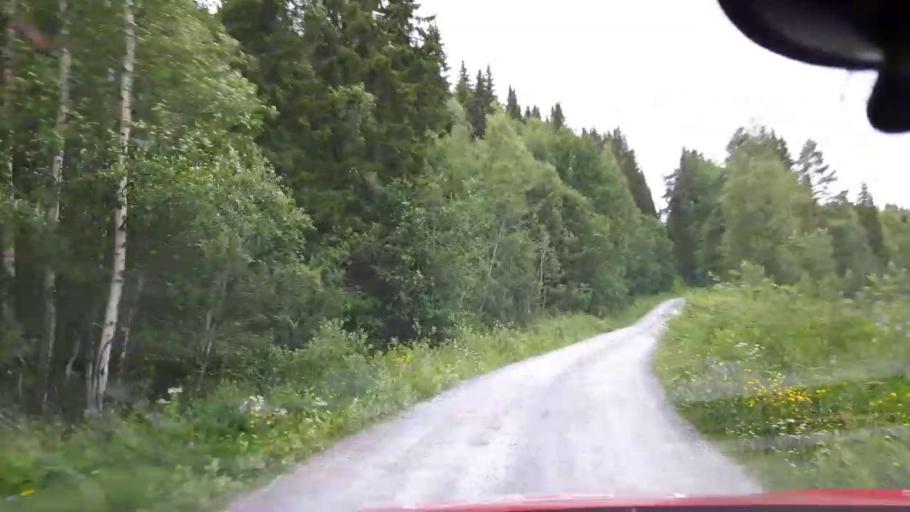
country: SE
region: Jaemtland
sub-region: OEstersunds Kommun
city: Brunflo
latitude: 63.0353
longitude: 14.9257
